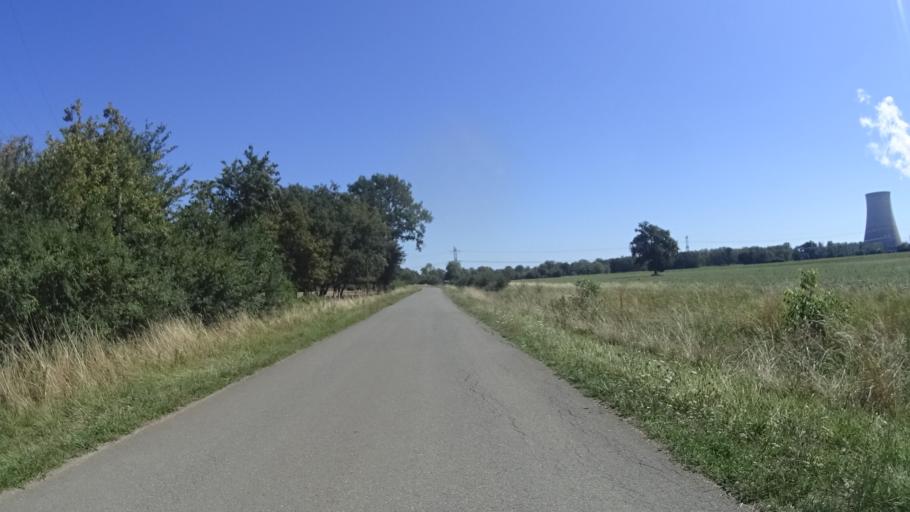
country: FR
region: Centre
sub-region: Departement du Cher
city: Belleville-sur-Loire
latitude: 47.5200
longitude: 2.8554
